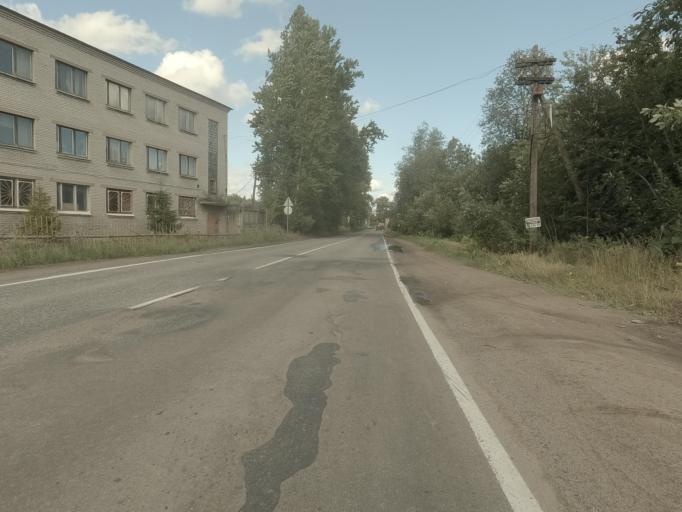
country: RU
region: Leningrad
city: Vsevolozhsk
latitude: 60.0230
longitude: 30.6957
